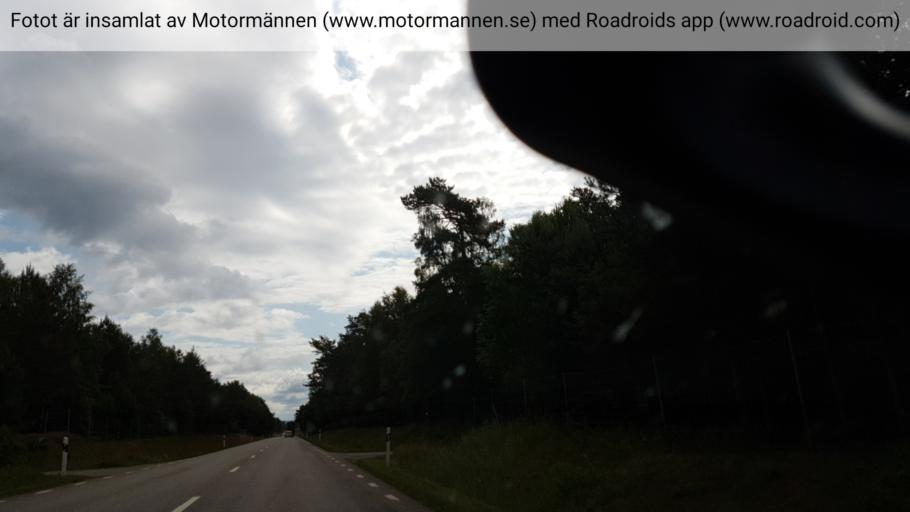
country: SE
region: Vaestra Goetaland
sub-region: Vara Kommun
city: Kvanum
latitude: 58.2128
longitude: 13.2440
